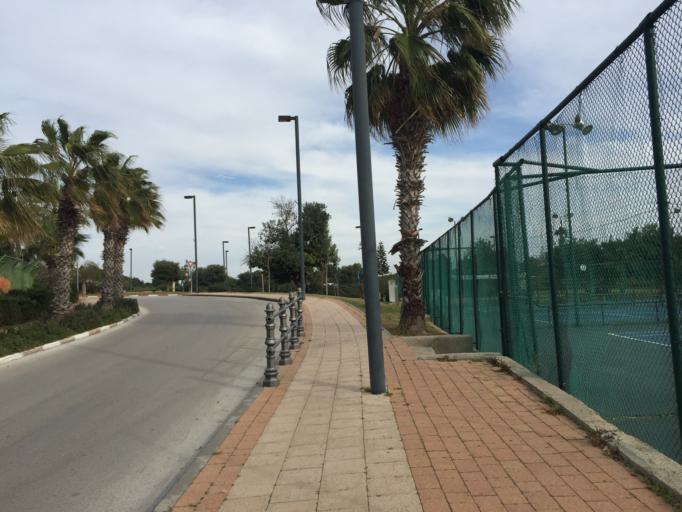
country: IL
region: Haifa
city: Qesarya
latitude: 32.5116
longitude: 34.9044
